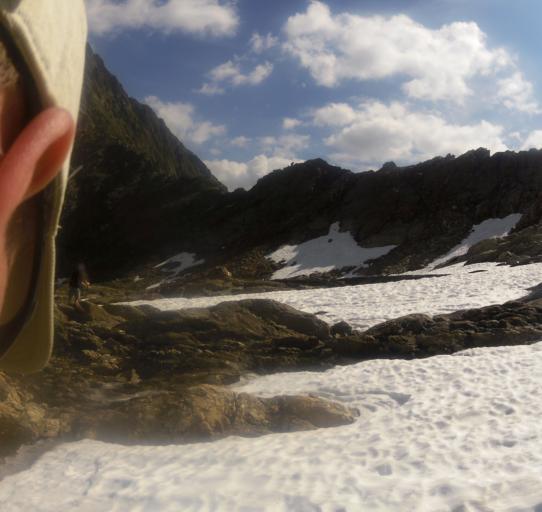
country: IT
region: Trentino-Alto Adige
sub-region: Bolzano
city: Racines
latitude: 46.9904
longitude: 11.2440
